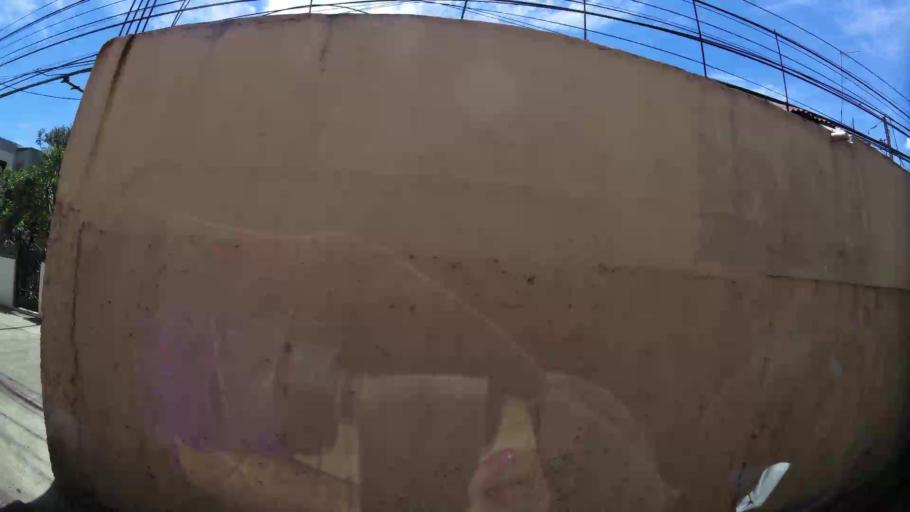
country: DO
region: Santiago
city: Santiago de los Caballeros
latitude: 19.4485
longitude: -70.6970
